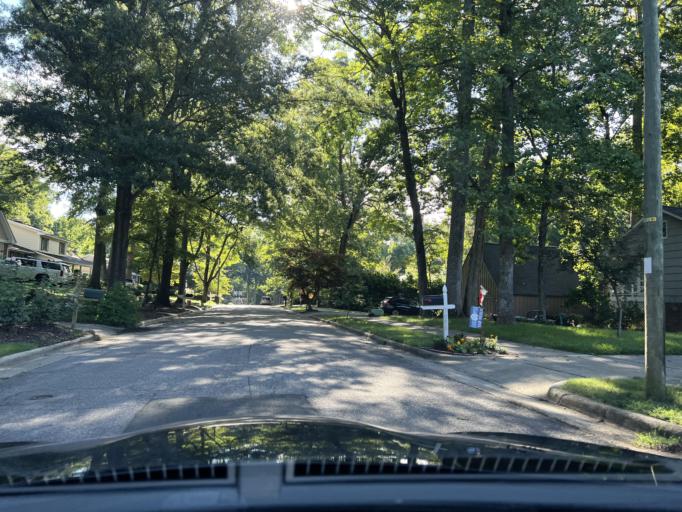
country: US
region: North Carolina
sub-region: Wake County
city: West Raleigh
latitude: 35.8439
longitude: -78.6210
